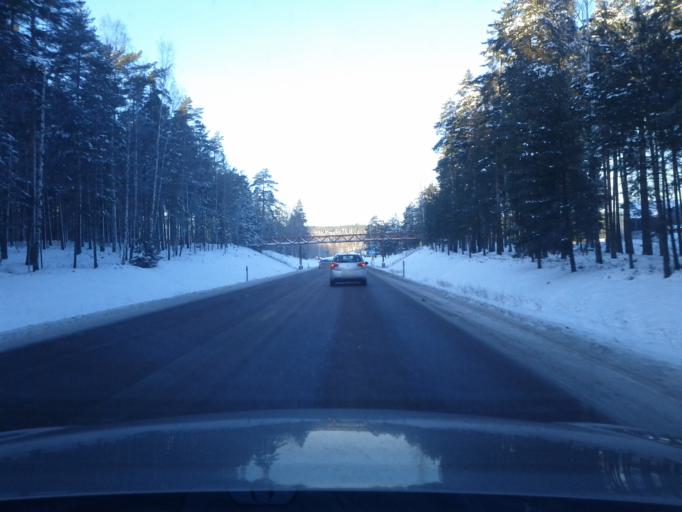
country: SE
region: Dalarna
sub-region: Faluns Kommun
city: Falun
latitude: 60.6164
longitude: 15.6495
